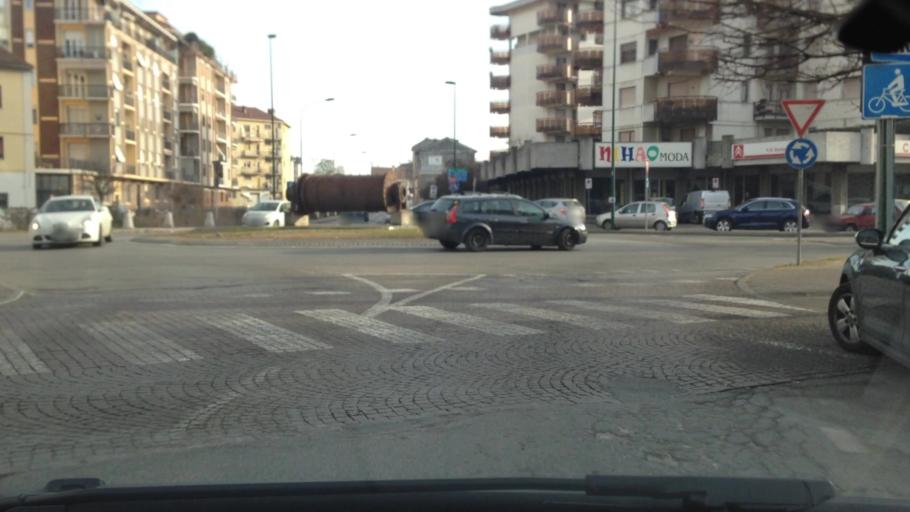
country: IT
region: Piedmont
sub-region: Provincia di Alessandria
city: Casale Monferrato
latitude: 45.1305
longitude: 8.4484
